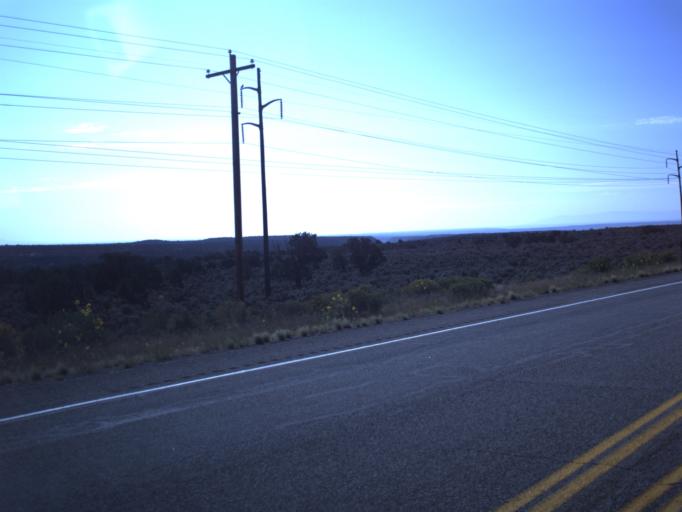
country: US
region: Utah
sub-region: San Juan County
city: Blanding
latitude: 37.5324
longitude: -109.4942
